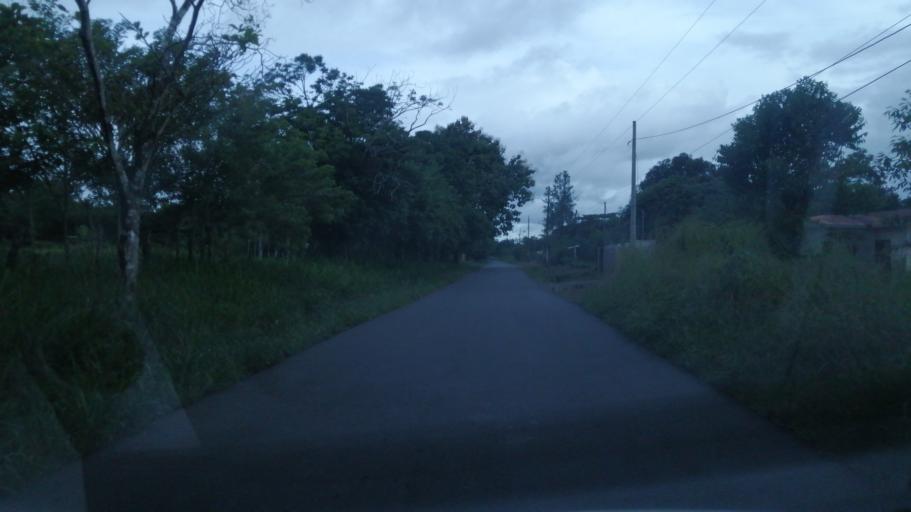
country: PA
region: Chiriqui
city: Tijera
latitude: 8.4527
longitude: -82.5255
